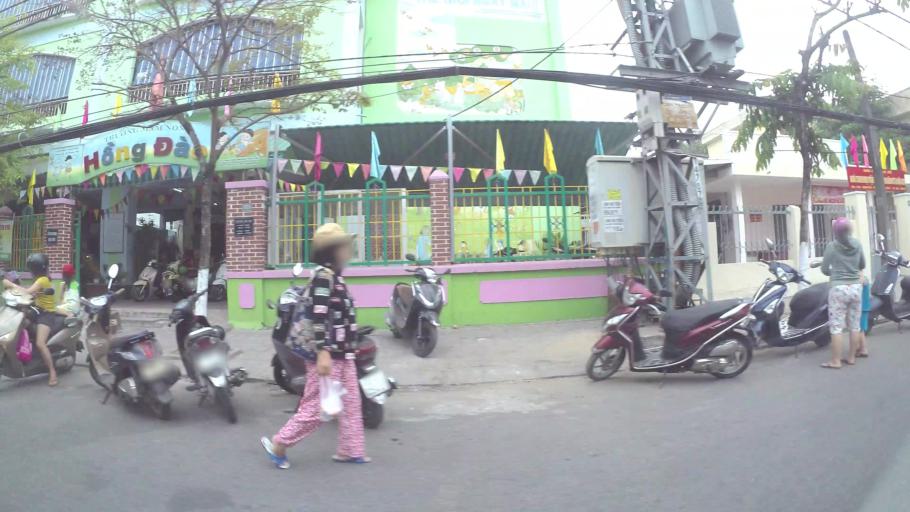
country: VN
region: Da Nang
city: Thanh Khe
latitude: 16.0525
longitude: 108.1847
